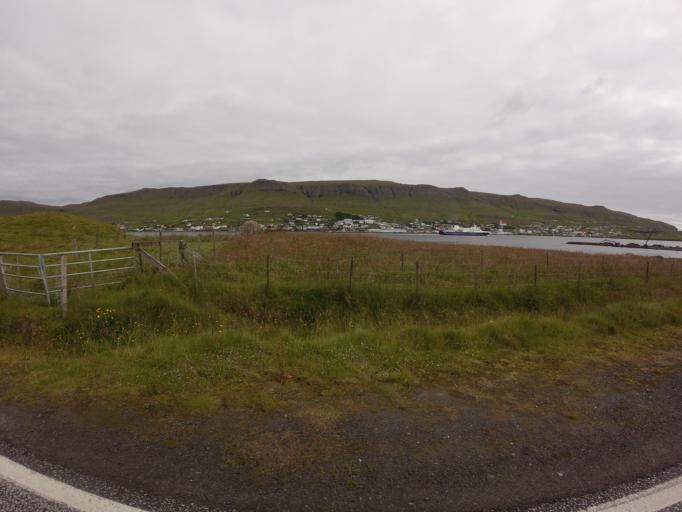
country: FO
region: Suduroy
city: Tvoroyri
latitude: 61.5491
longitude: -6.8239
